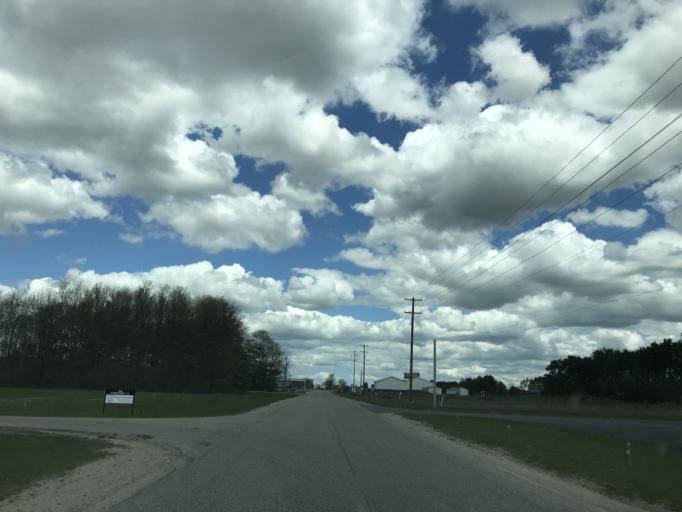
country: US
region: Michigan
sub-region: Otsego County
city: Gaylord
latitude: 45.0327
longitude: -84.6917
